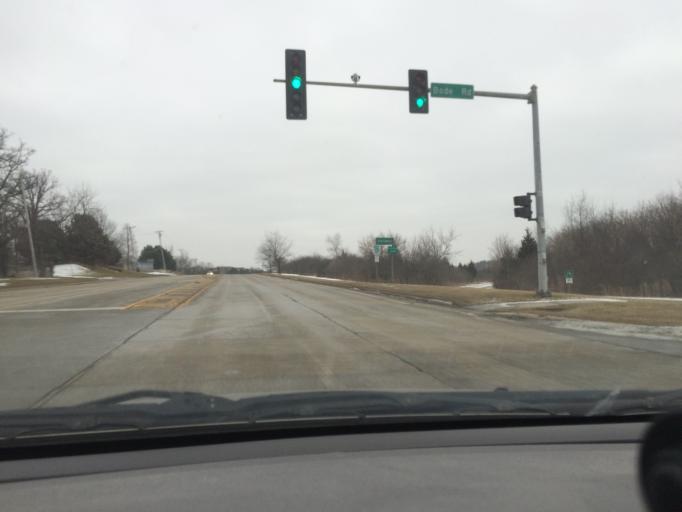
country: US
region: Illinois
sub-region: Cook County
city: Streamwood
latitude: 42.0391
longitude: -88.1791
